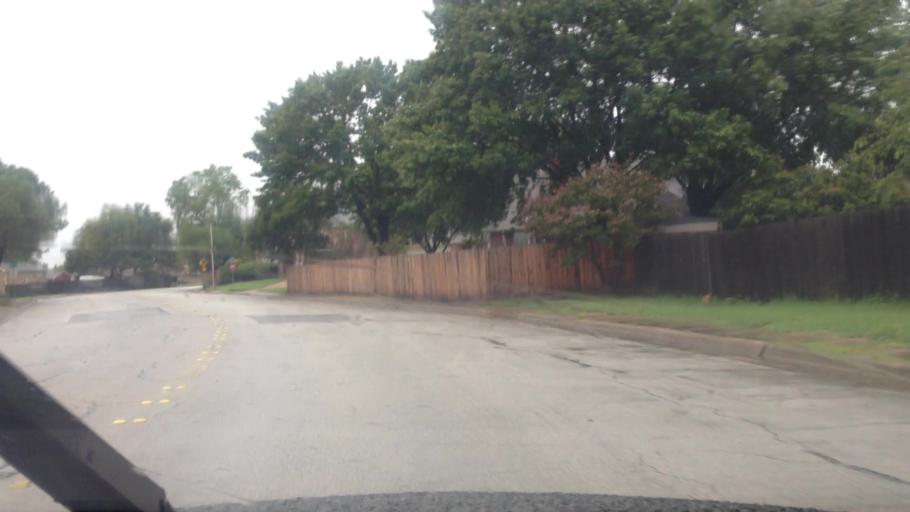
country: US
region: Texas
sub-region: Tarrant County
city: North Richland Hills
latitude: 32.8643
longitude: -97.2184
